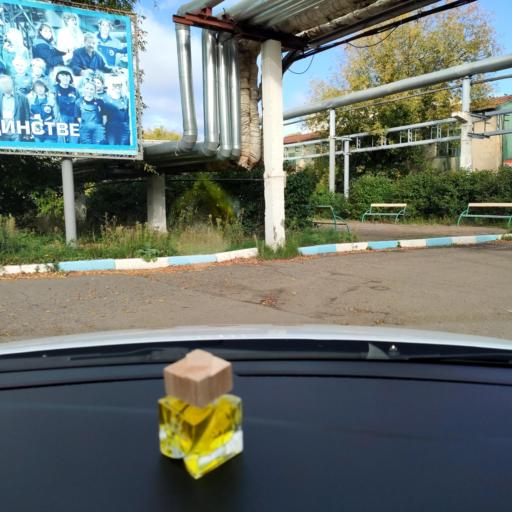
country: RU
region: Tatarstan
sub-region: Gorod Kazan'
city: Kazan
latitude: 55.7553
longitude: 49.1222
